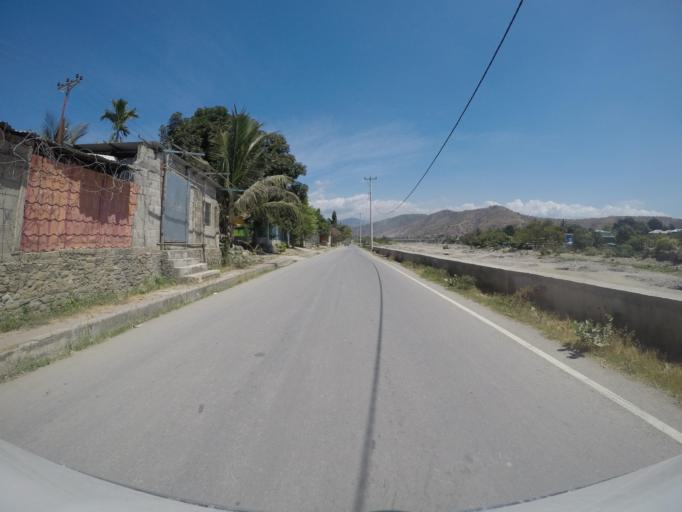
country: TL
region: Dili
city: Dili
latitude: -8.5560
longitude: 125.5364
